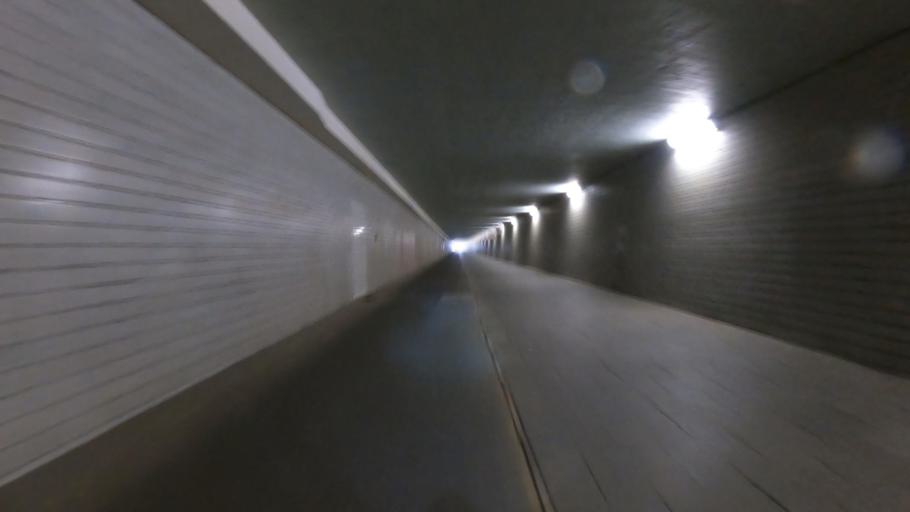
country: DE
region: Hamburg
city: Langenhorn
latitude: 53.6478
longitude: 9.9797
